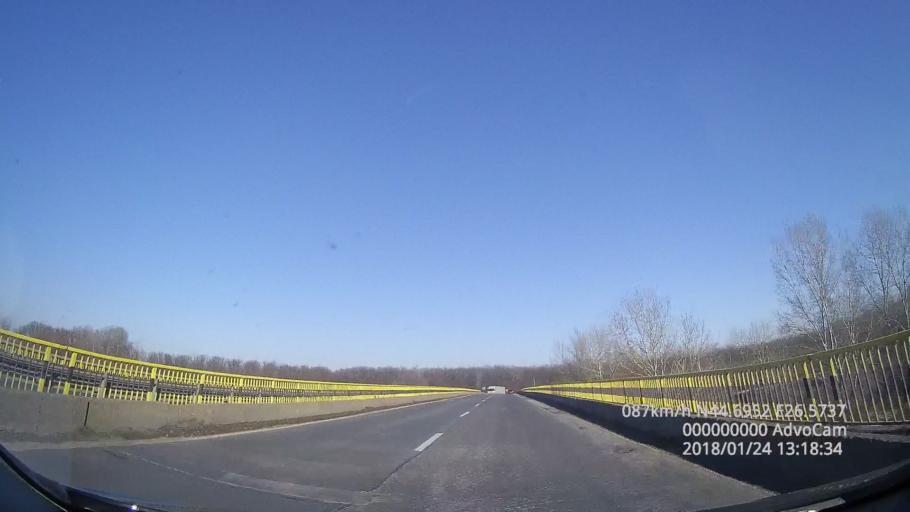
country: RO
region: Ialomita
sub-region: Comuna Cosereni
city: Cosereni
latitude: 44.6958
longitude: 26.5739
